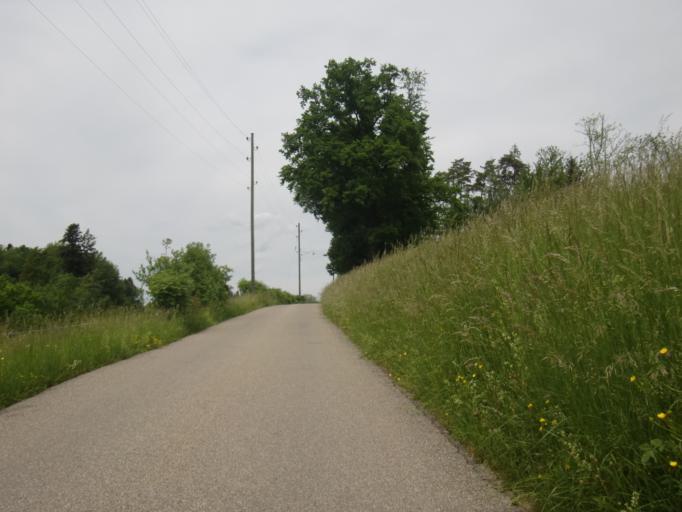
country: CH
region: Zurich
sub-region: Bezirk Hinwil
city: Durnten
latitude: 47.2819
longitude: 8.8400
